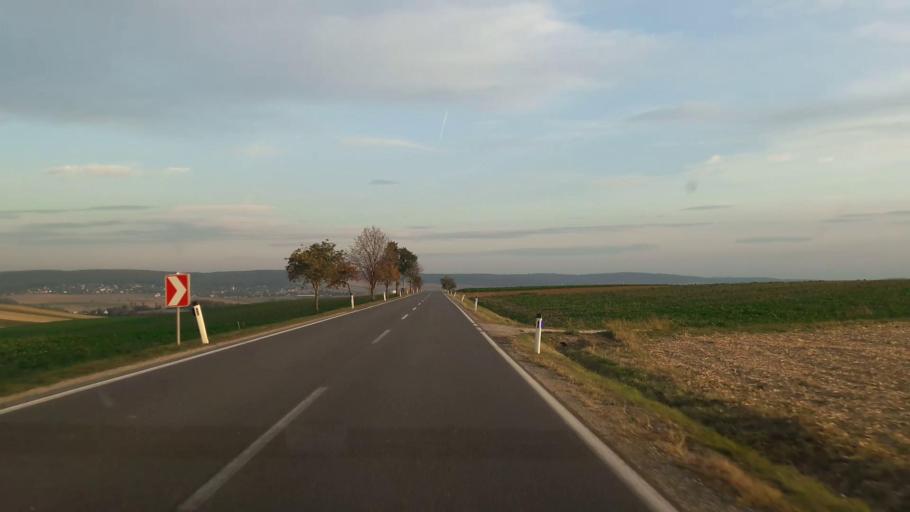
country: AT
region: Lower Austria
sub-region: Politischer Bezirk Korneuburg
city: Grossrussbach
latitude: 48.4507
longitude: 16.3813
